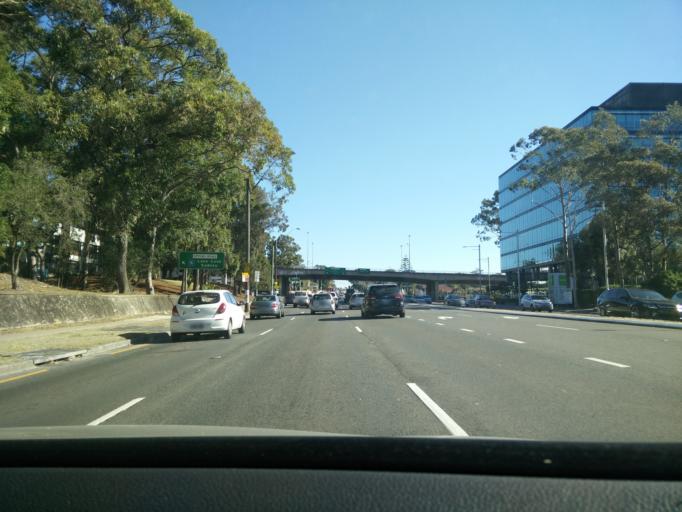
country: AU
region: New South Wales
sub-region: Ryde
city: North Ryde
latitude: -33.7865
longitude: 151.1271
